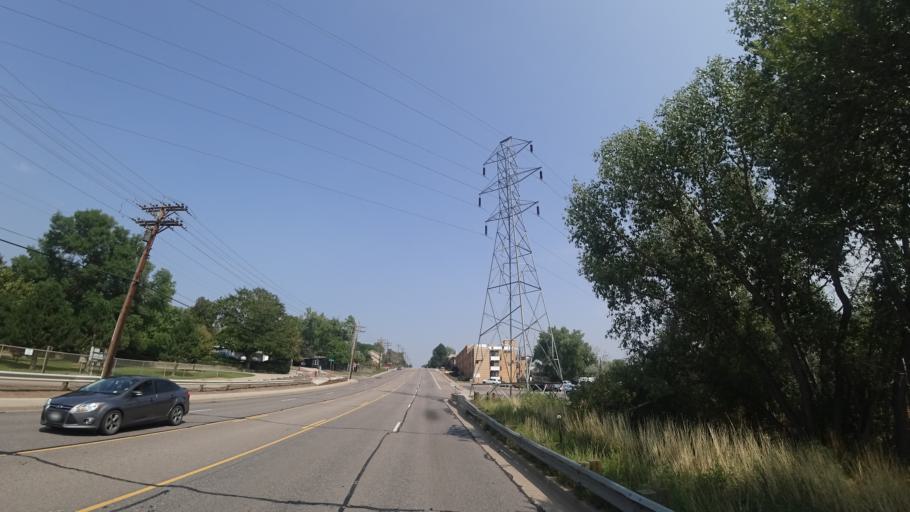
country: US
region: Colorado
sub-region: Arapahoe County
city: Littleton
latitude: 39.6240
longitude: -104.9993
